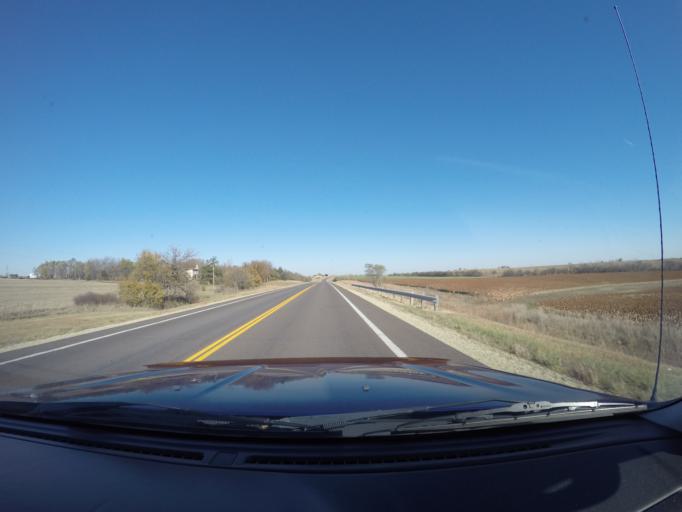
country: US
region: Kansas
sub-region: Marshall County
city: Blue Rapids
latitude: 39.5540
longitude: -96.7553
